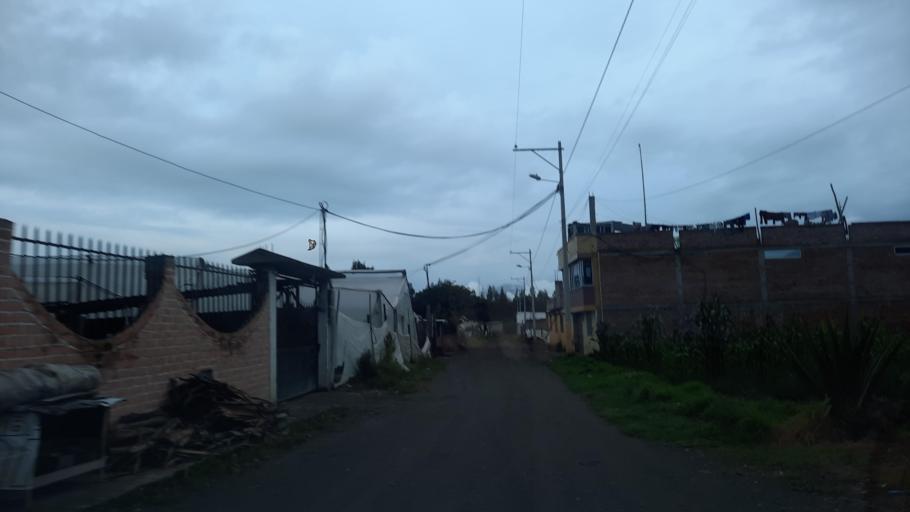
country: EC
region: Chimborazo
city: Riobamba
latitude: -1.6857
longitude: -78.6618
